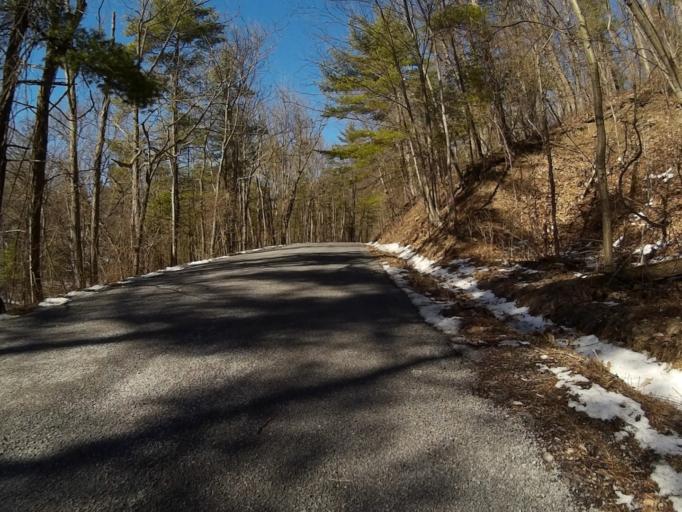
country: US
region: Pennsylvania
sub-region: Centre County
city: Stormstown
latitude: 40.8414
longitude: -78.0251
